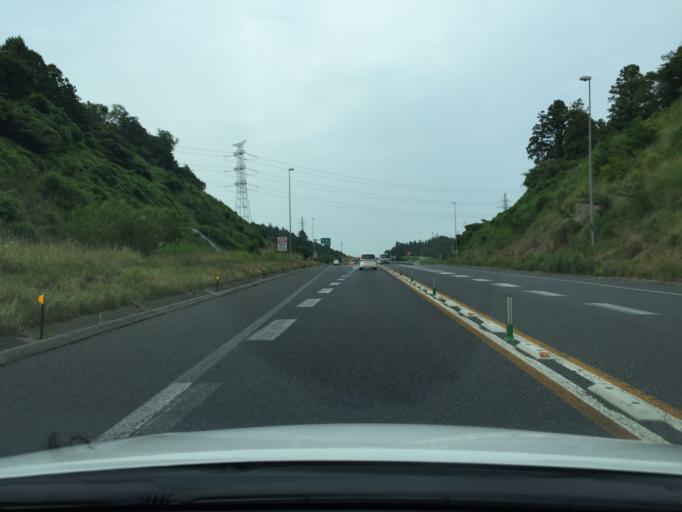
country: JP
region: Fukushima
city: Iwaki
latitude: 37.2346
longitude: 140.9817
